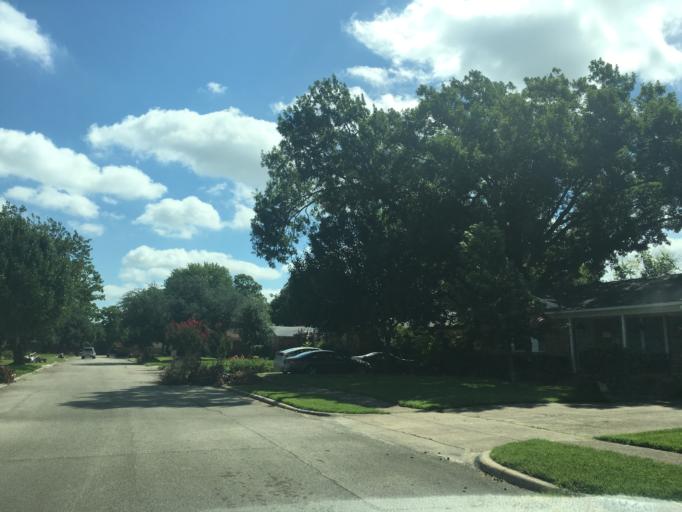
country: US
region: Texas
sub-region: Dallas County
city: Garland
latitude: 32.8417
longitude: -96.6556
